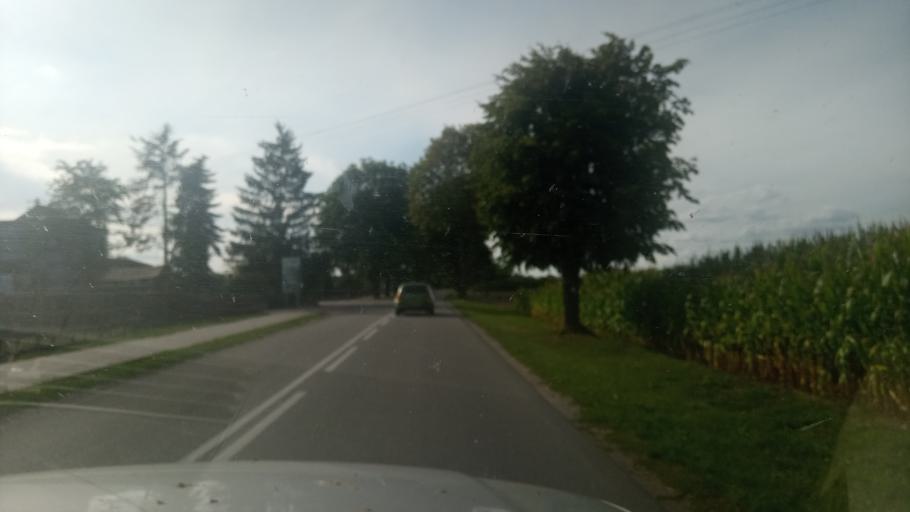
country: PL
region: Greater Poland Voivodeship
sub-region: Powiat pilski
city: Lobzenica
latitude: 53.2536
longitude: 17.2689
